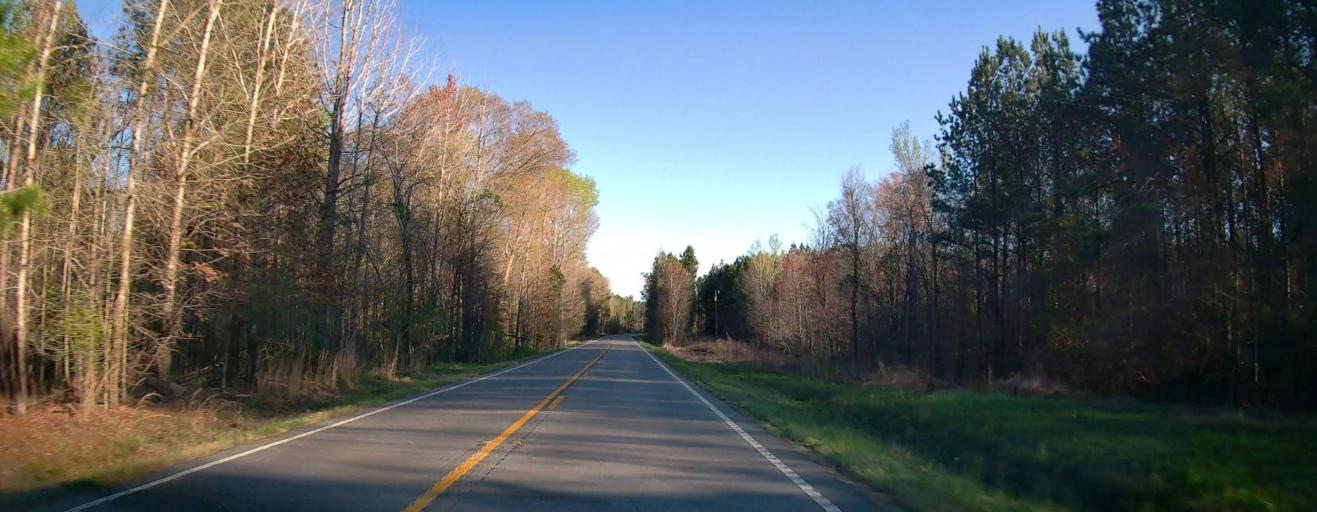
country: US
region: Georgia
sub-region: Pulaski County
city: Hawkinsville
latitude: 32.1996
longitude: -83.3733
